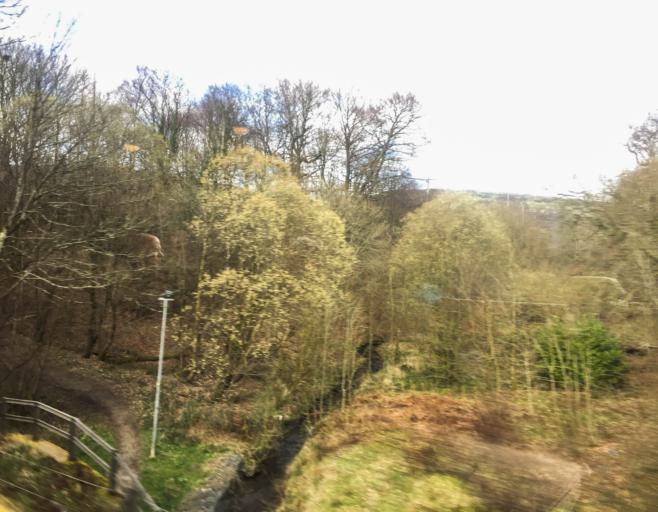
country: GB
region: Scotland
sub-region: West Dunbartonshire
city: Old Kilpatrick
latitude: 55.9228
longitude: -4.4507
